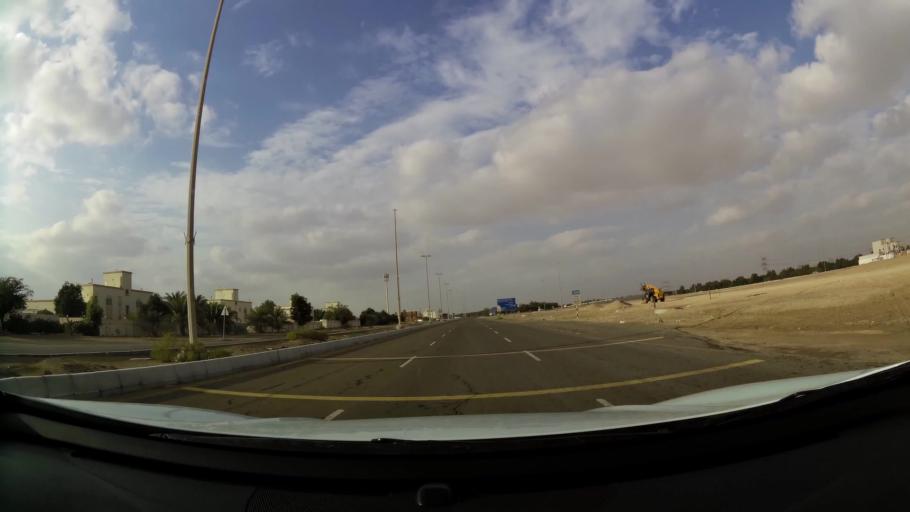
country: AE
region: Abu Dhabi
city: Abu Dhabi
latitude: 24.3455
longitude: 54.5663
